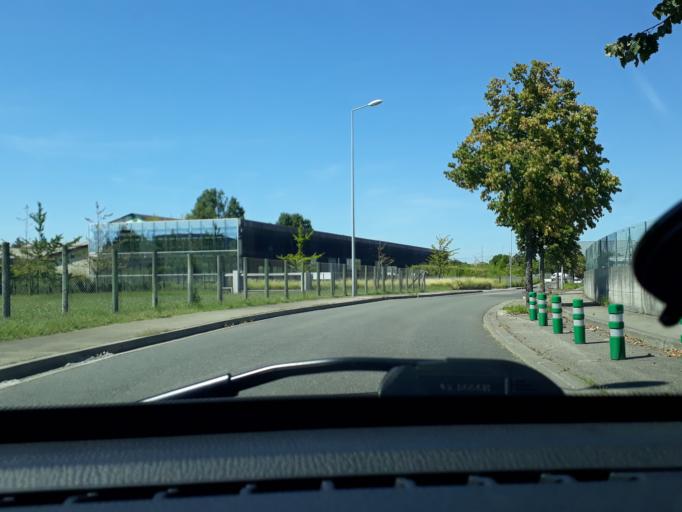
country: FR
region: Rhone-Alpes
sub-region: Departement du Rhone
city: Saint-Priest
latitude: 45.6964
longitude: 4.9192
